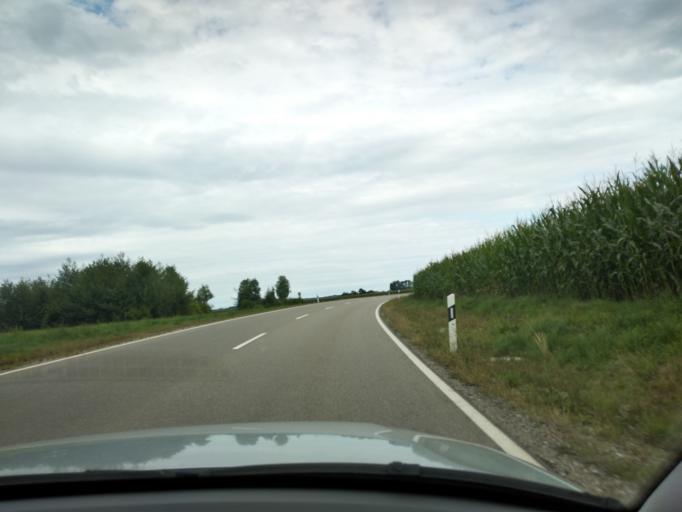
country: DE
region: Bavaria
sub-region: Swabia
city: Trunkelsberg
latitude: 47.9973
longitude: 10.2151
